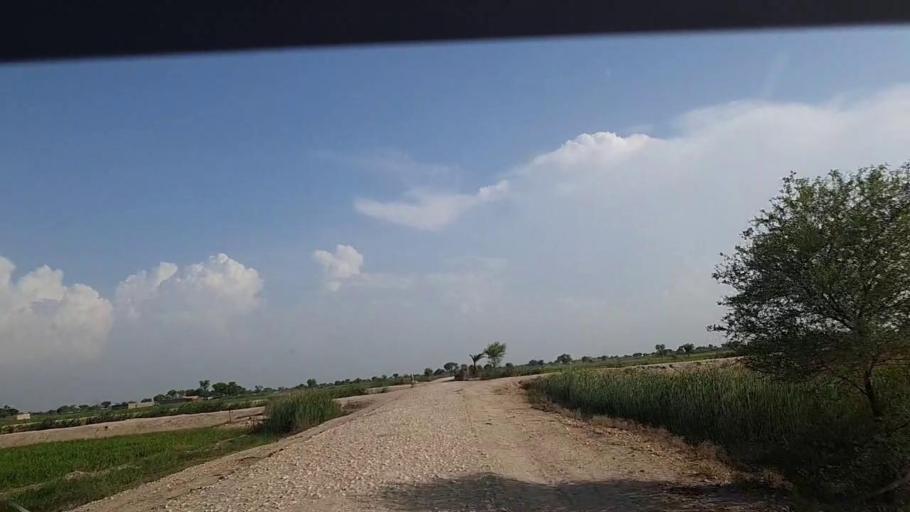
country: PK
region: Sindh
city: Khanpur
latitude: 27.8513
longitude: 69.3775
